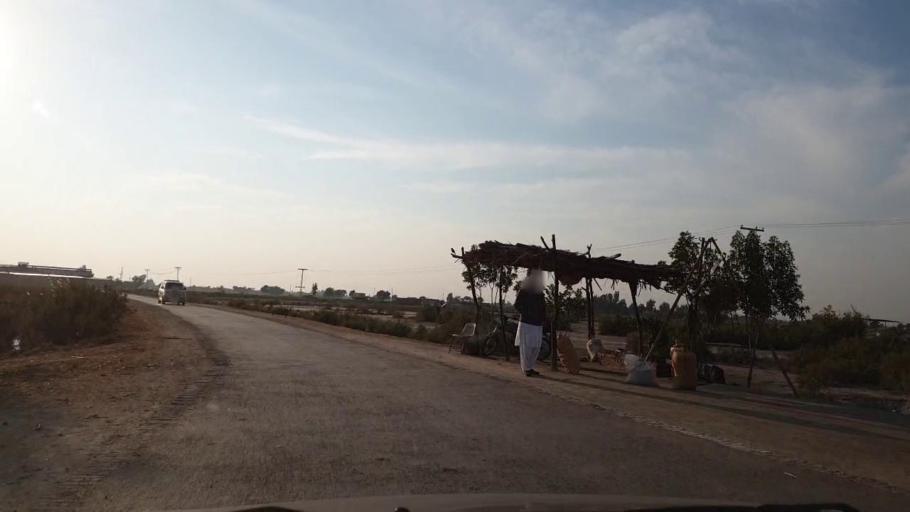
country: PK
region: Sindh
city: Khadro
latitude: 26.1550
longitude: 68.7299
